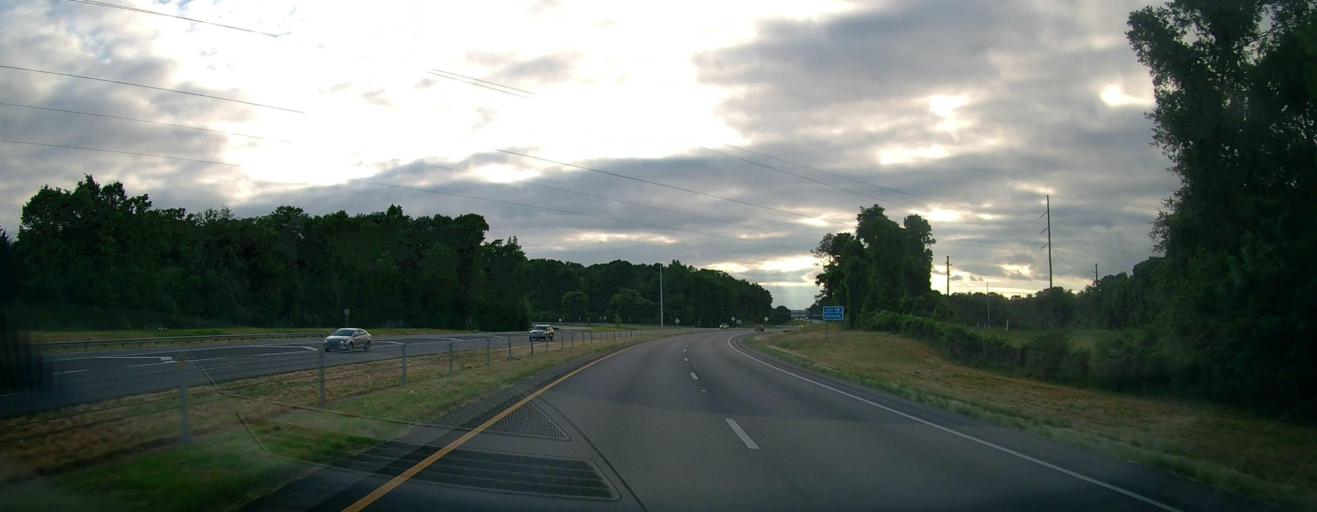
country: US
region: Georgia
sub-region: Clarke County
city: Country Club Estates
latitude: 33.9706
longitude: -83.4032
